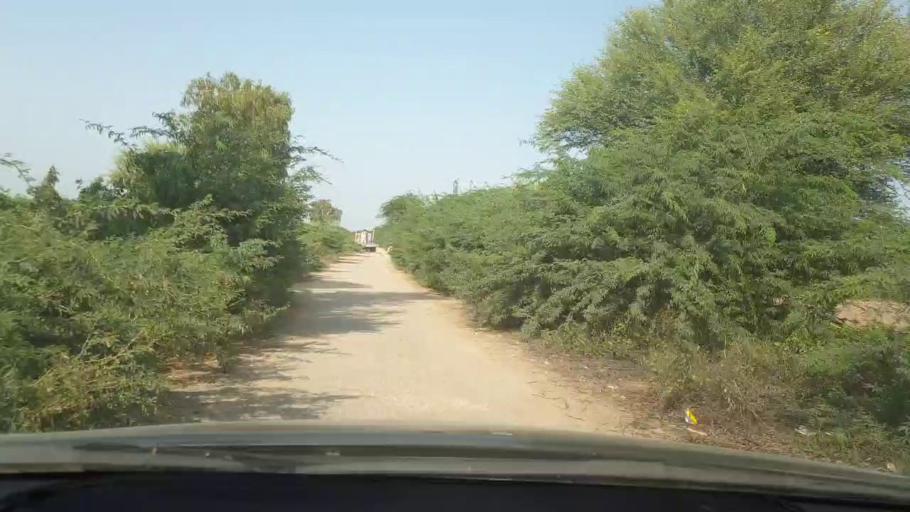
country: PK
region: Sindh
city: Naukot
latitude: 24.7689
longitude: 69.2555
